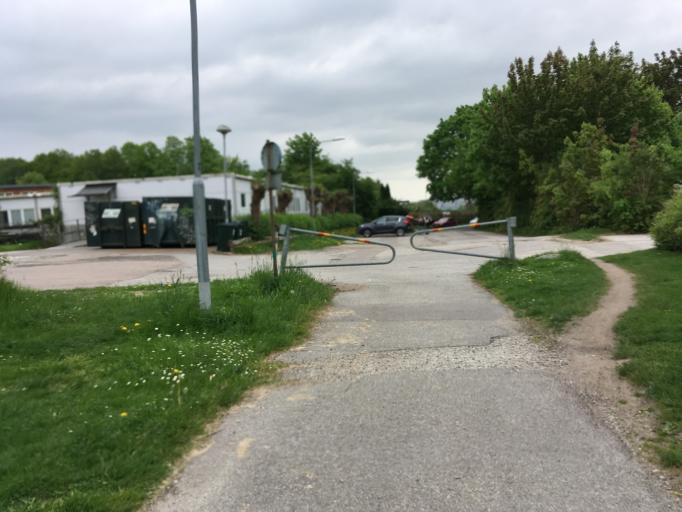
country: SE
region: Skane
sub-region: Lunds Kommun
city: Lund
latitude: 55.6995
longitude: 13.1701
